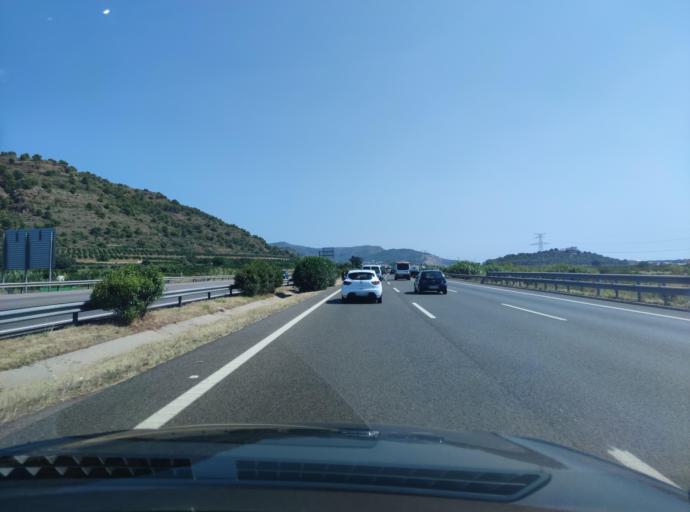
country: ES
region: Valencia
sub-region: Provincia de Valencia
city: Petres
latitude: 39.6811
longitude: -0.2982
